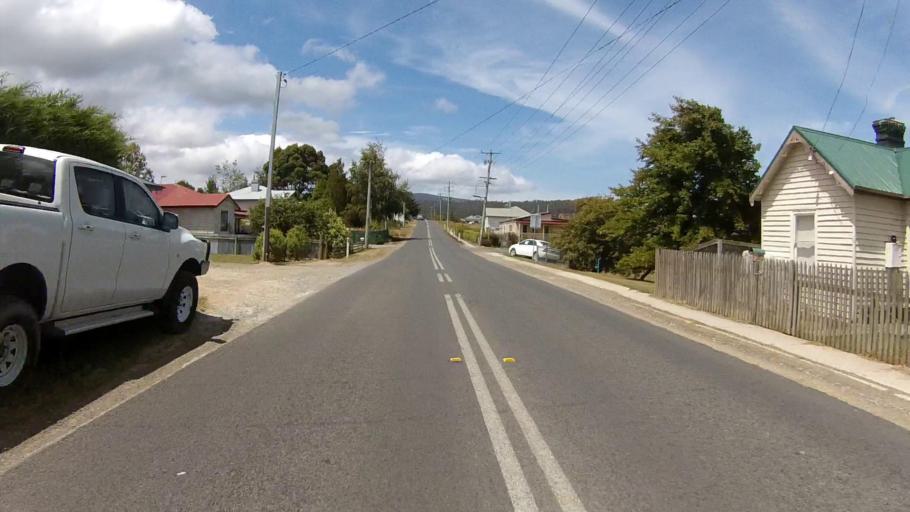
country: AU
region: Tasmania
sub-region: Huon Valley
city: Cygnet
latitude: -43.1641
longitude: 147.0862
